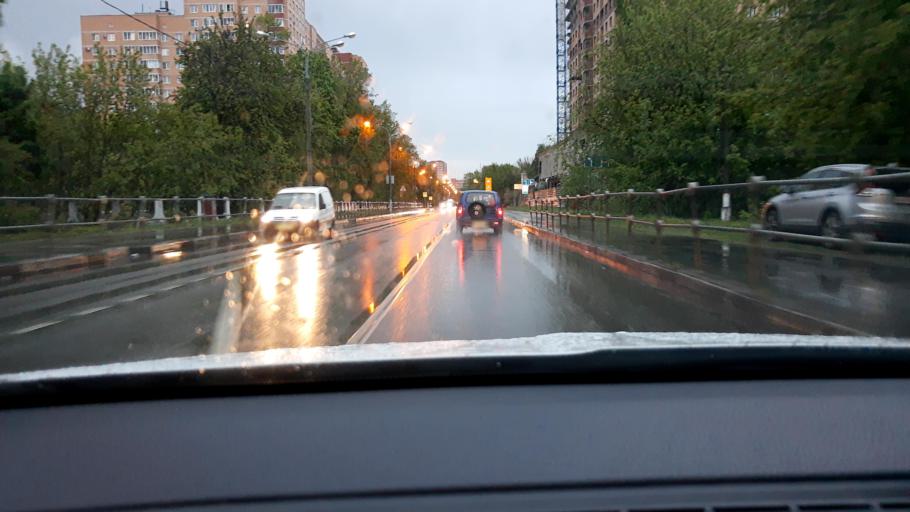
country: RU
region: Moskovskaya
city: Shchelkovo
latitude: 55.9194
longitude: 37.9809
